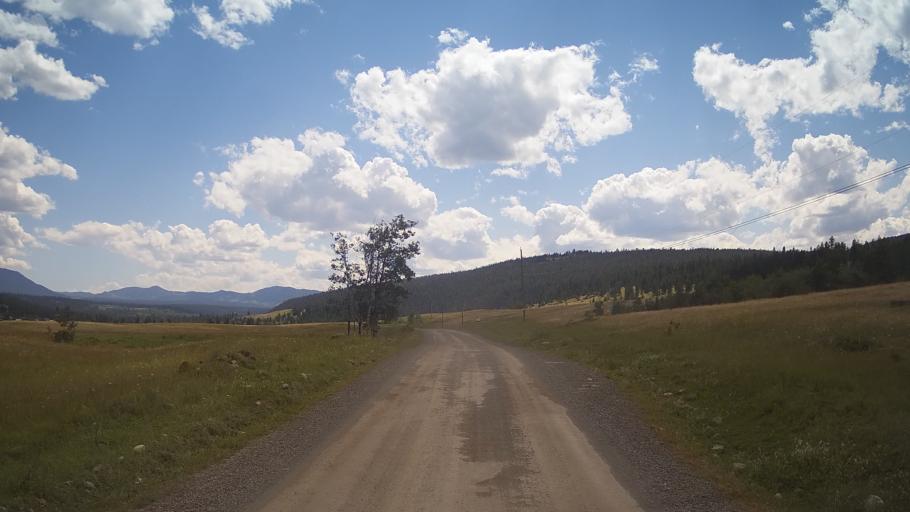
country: CA
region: British Columbia
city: Lillooet
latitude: 51.3148
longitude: -121.9831
